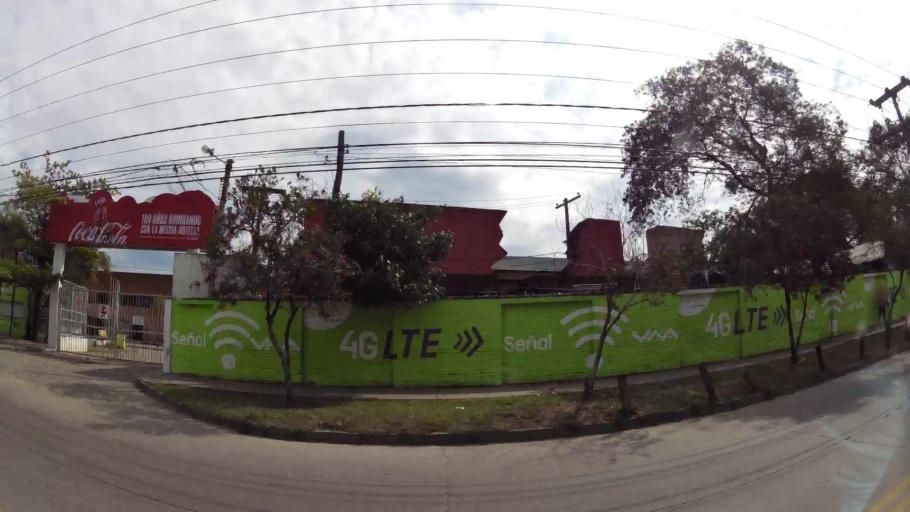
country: BO
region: Santa Cruz
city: Santa Cruz de la Sierra
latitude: -17.7834
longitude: -63.2061
